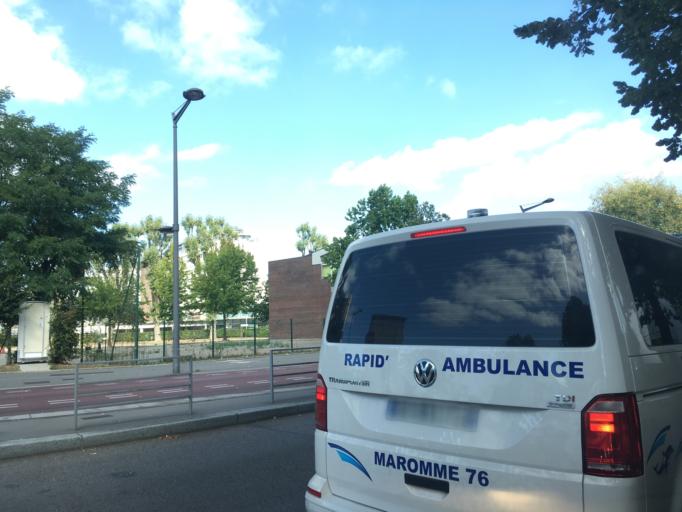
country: FR
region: Haute-Normandie
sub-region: Departement de la Seine-Maritime
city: Rouen
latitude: 49.4380
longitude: 1.1059
